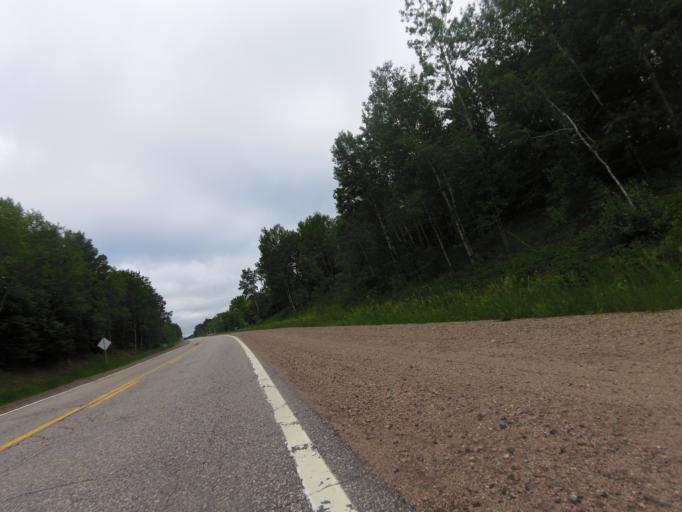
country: CA
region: Quebec
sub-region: Outaouais
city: Shawville
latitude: 45.9118
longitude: -76.3166
